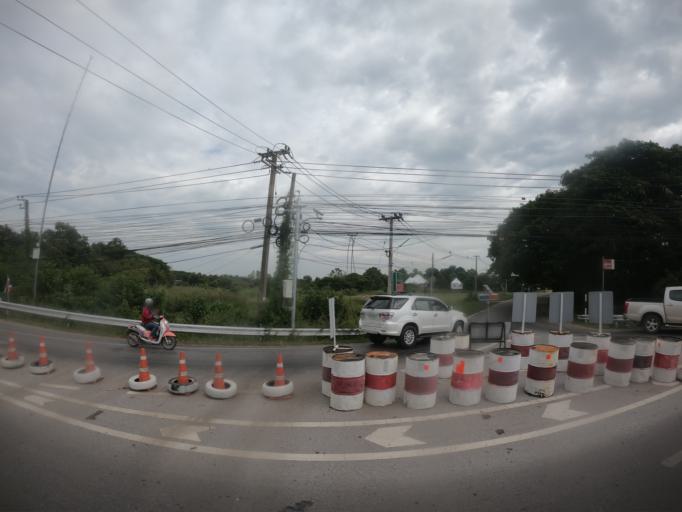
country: TH
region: Maha Sarakham
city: Maha Sarakham
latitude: 16.2007
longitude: 103.2925
